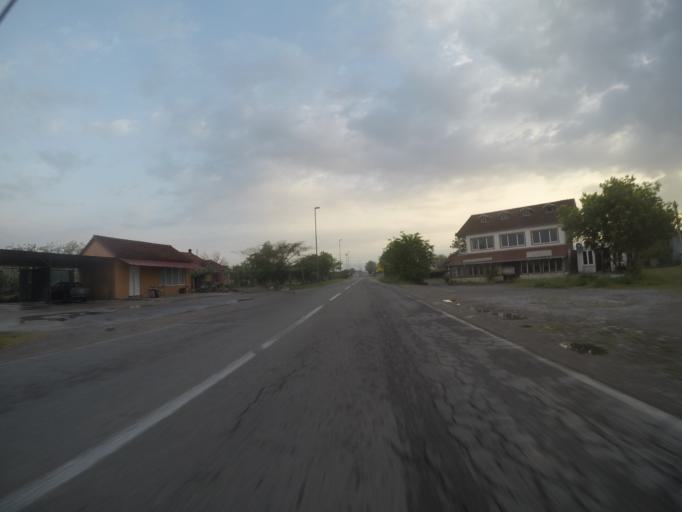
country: ME
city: Mojanovici
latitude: 42.3420
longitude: 19.2217
